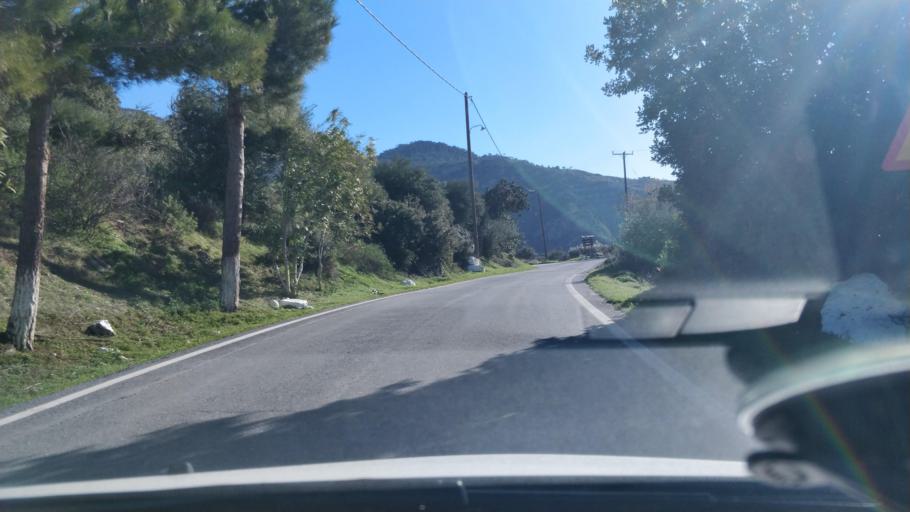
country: GR
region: Crete
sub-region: Nomos Lasithiou
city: Kritsa
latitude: 35.0796
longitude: 25.5906
